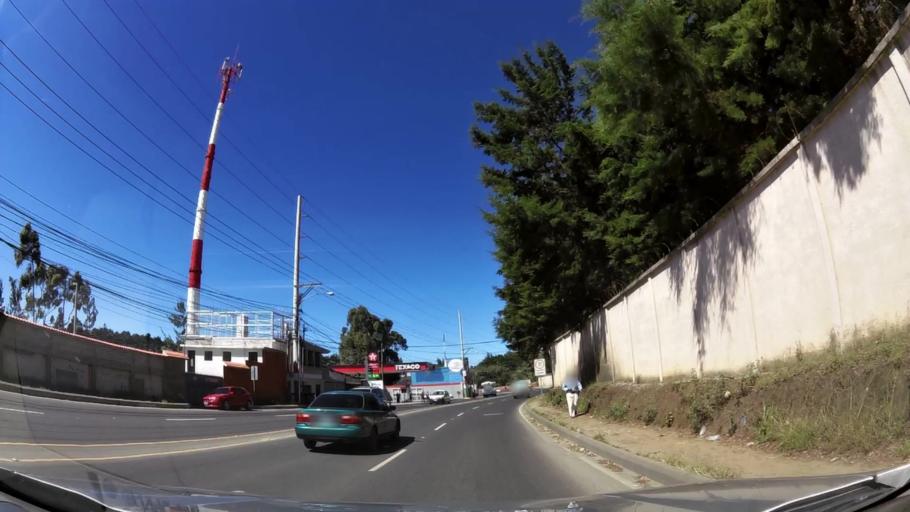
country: GT
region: Guatemala
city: San Jose Pinula
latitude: 14.5439
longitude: -90.4420
